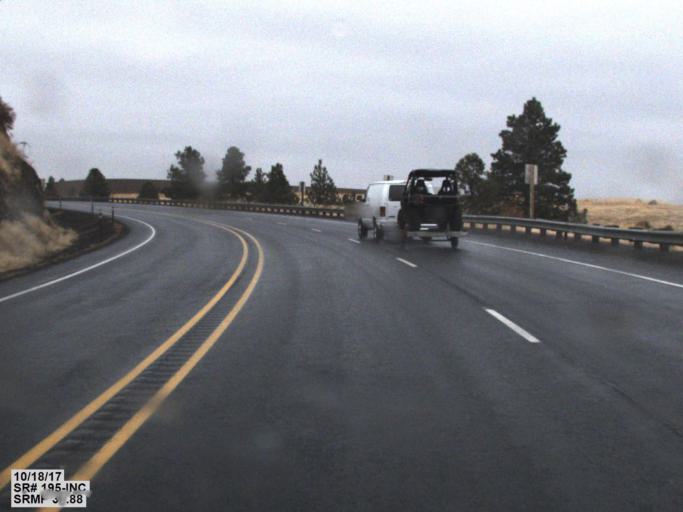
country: US
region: Washington
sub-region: Whitman County
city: Colfax
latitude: 46.9046
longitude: -117.3478
